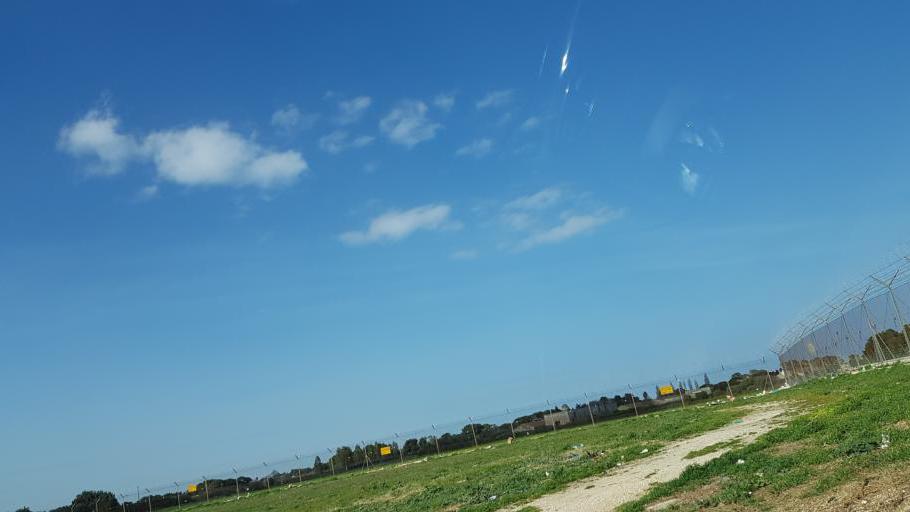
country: IT
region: Apulia
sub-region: Provincia di Brindisi
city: Brindisi
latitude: 40.6507
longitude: 17.9371
